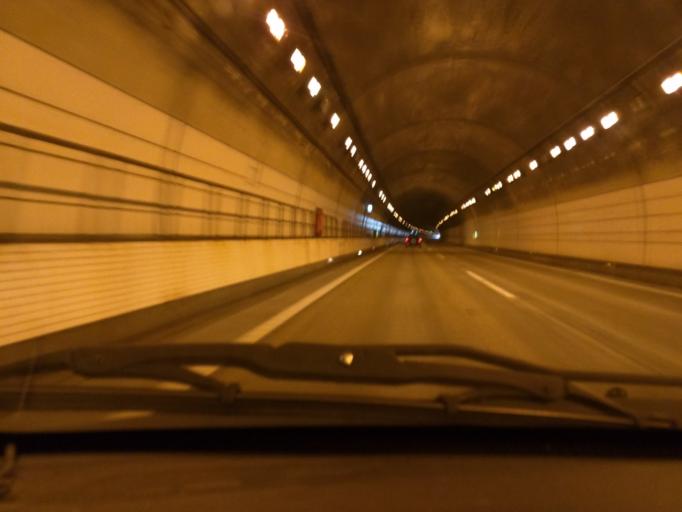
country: JP
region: Nagano
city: Nakano
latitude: 36.7992
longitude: 138.2840
